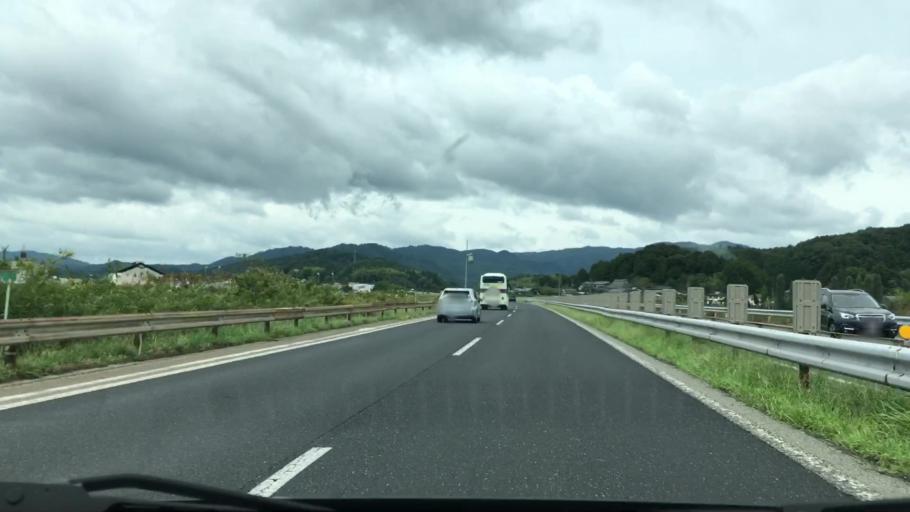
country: JP
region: Okayama
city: Tsuyama
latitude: 35.0595
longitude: 133.9078
